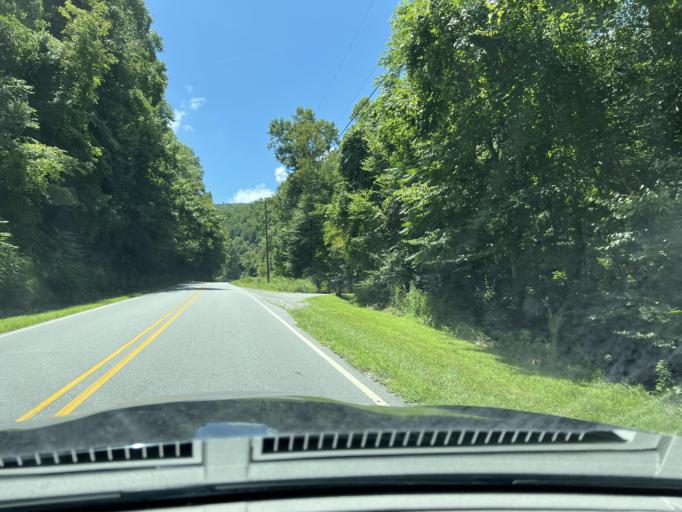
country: US
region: North Carolina
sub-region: Henderson County
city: Fruitland
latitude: 35.4243
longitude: -82.4192
